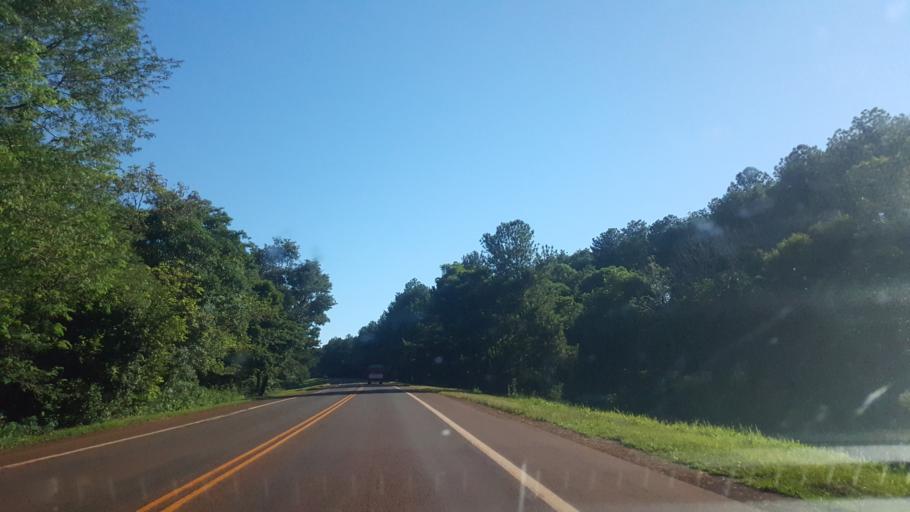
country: AR
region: Misiones
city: Puerto Libertad
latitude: -25.9074
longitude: -54.5683
